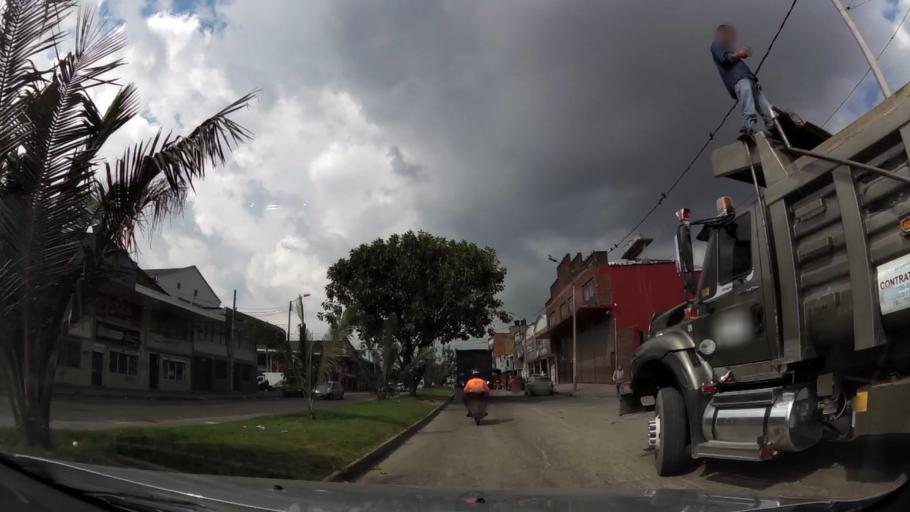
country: CO
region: Bogota D.C.
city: Bogota
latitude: 4.6105
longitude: -74.0863
